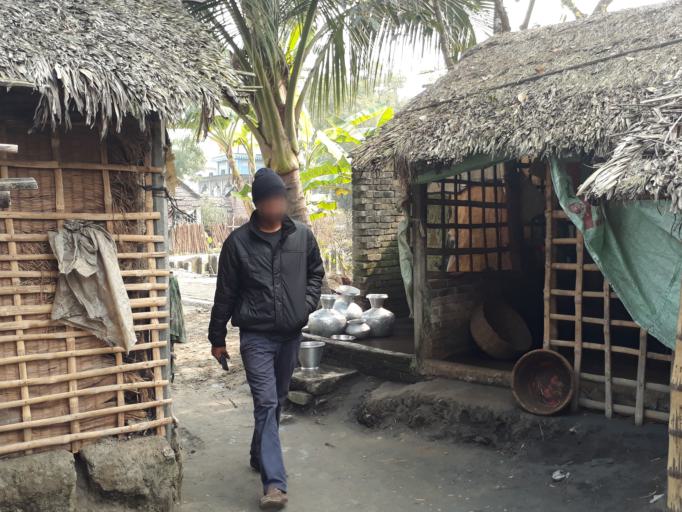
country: BD
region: Khulna
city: Kesabpur
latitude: 22.7906
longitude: 89.2736
